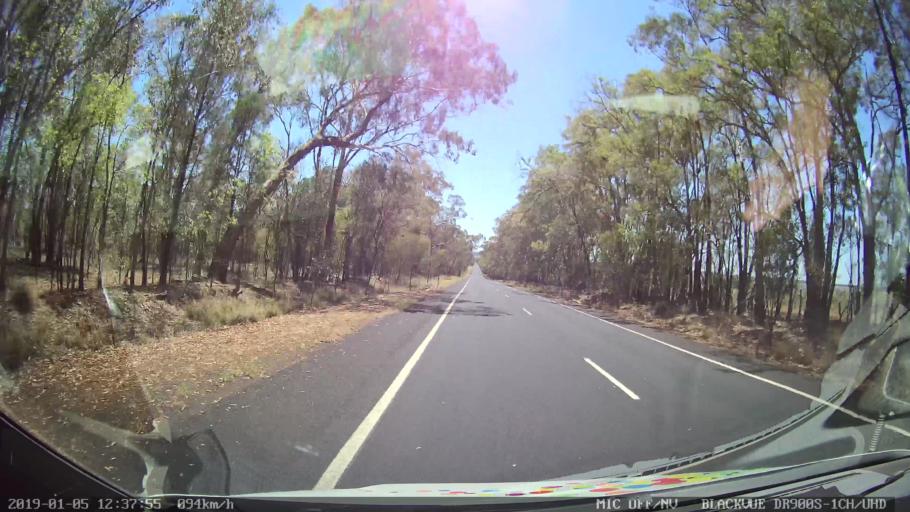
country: AU
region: New South Wales
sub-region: Warrumbungle Shire
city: Coonabarabran
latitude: -31.2000
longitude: 149.4614
